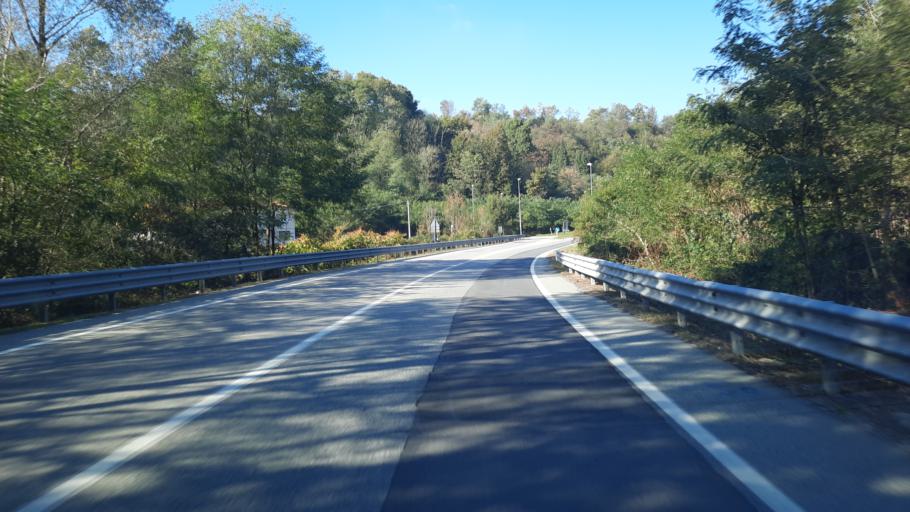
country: IT
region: Piedmont
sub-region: Provincia di Novara
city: Gozzano
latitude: 45.7420
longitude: 8.4246
